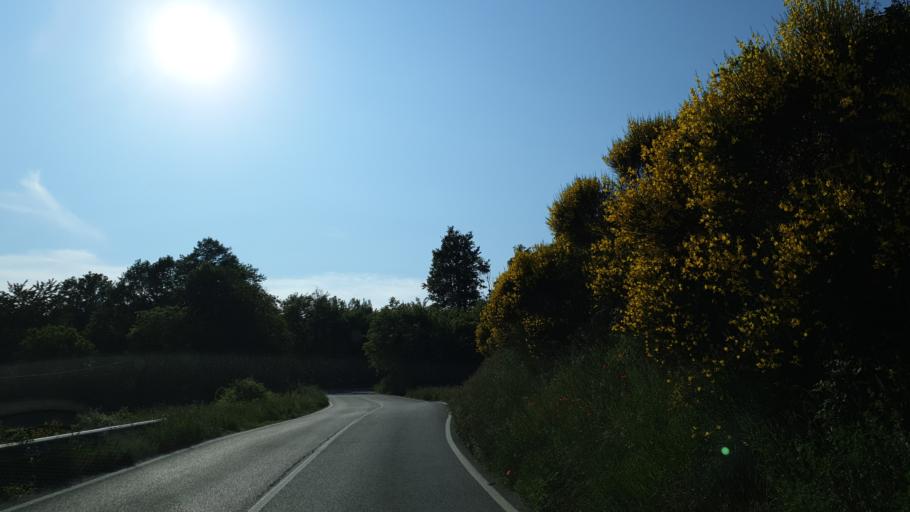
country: IT
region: Tuscany
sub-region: Province of Arezzo
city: Castel San Niccolo
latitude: 43.7711
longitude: 11.6961
